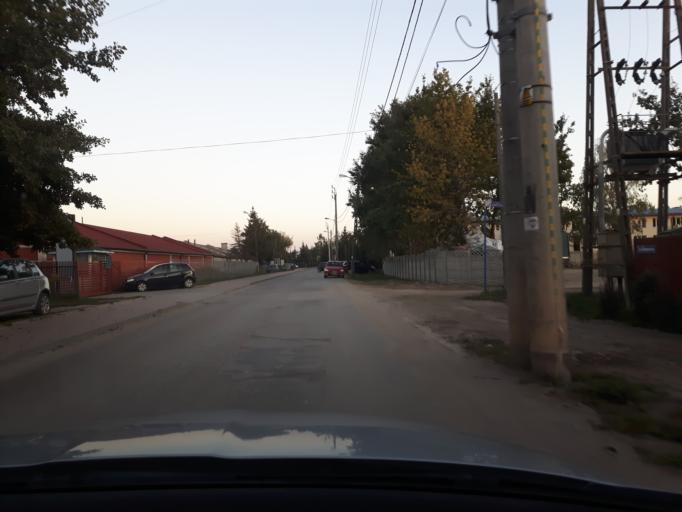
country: PL
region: Masovian Voivodeship
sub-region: Powiat wolominski
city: Kobylka
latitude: 52.3424
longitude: 21.1866
